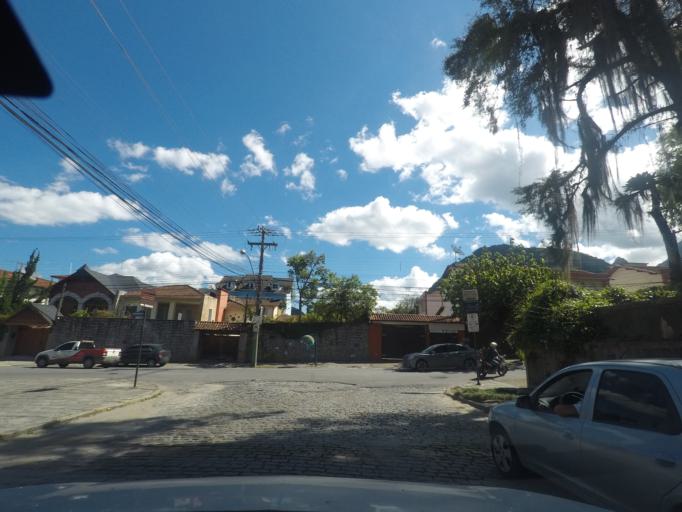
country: BR
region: Rio de Janeiro
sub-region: Teresopolis
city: Teresopolis
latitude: -22.4448
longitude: -42.9791
